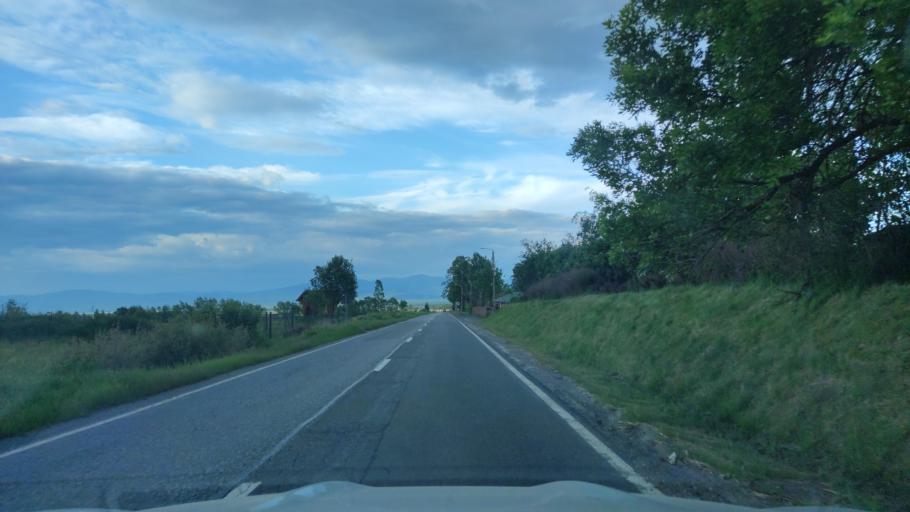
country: RO
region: Harghita
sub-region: Comuna Joseni
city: Joseni
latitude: 46.6835
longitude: 25.4084
